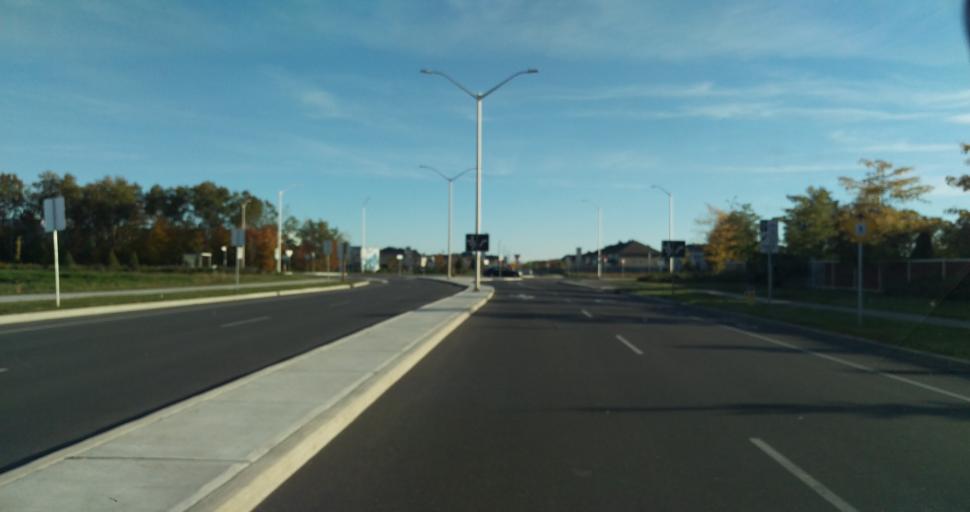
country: CA
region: Ontario
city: Clarence-Rockland
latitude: 45.4556
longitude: -75.4655
